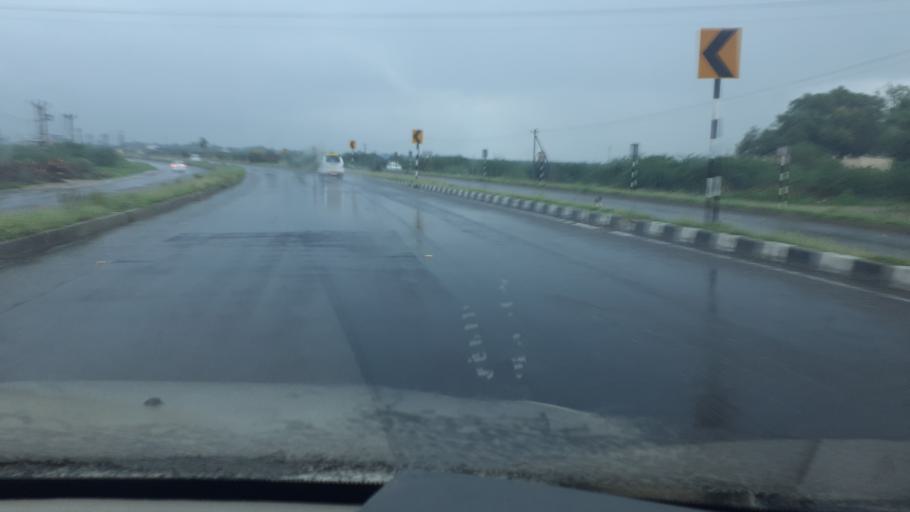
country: IN
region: Tamil Nadu
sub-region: Virudhunagar
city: Virudunagar
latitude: 9.5913
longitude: 77.9418
